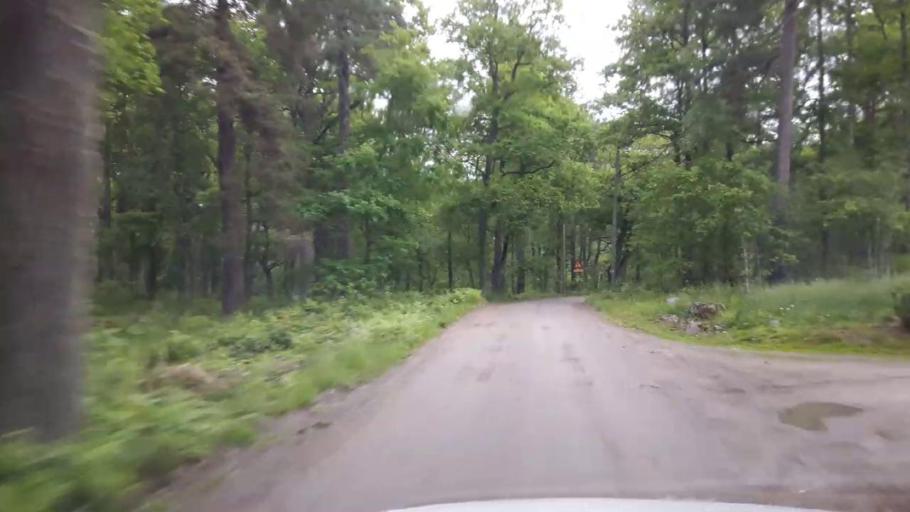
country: SE
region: Vaestmanland
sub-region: Arboga Kommun
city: Tyringe
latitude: 59.3813
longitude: 15.9407
